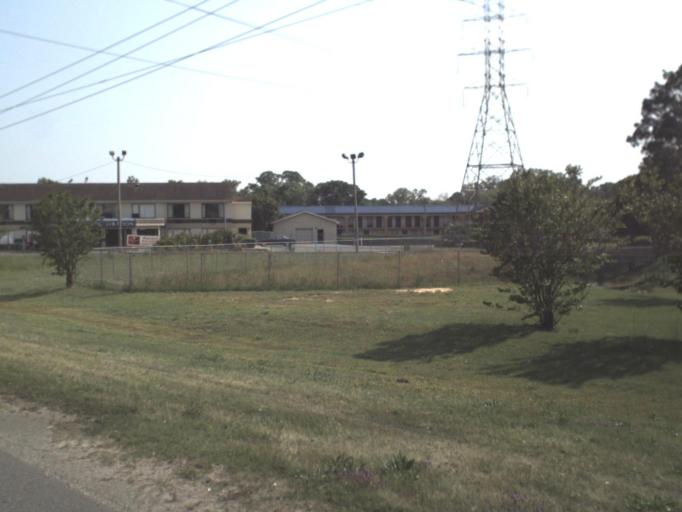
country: US
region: Florida
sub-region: Escambia County
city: Ensley
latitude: 30.4943
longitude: -87.2623
